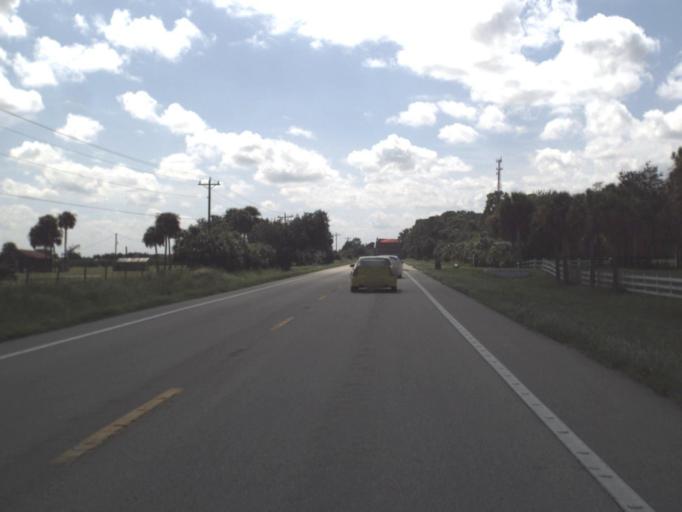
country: US
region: Florida
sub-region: Collier County
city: Immokalee
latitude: 26.5642
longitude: -81.4361
